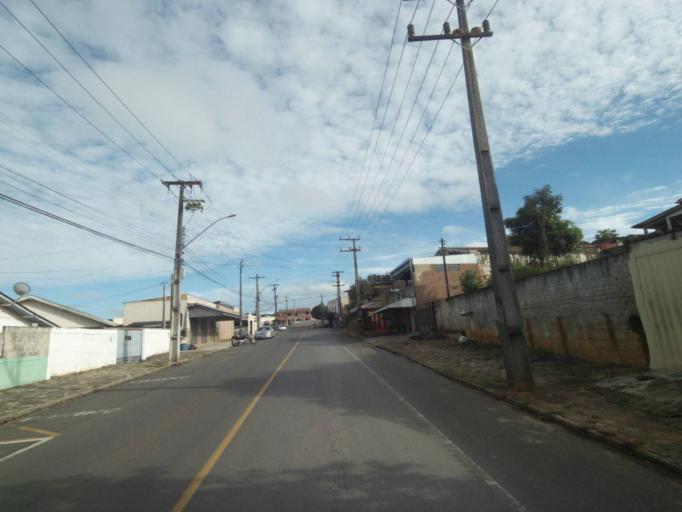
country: BR
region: Parana
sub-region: Telemaco Borba
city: Telemaco Borba
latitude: -24.3386
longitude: -50.6155
